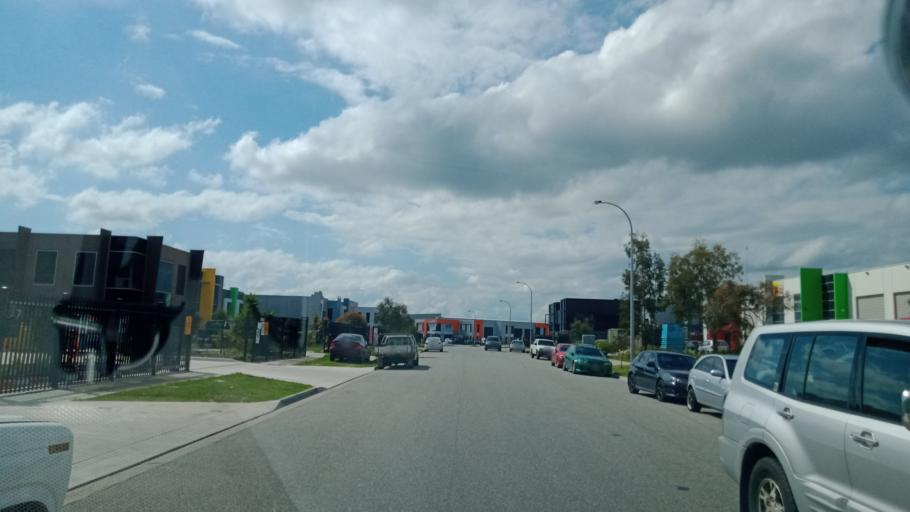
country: AU
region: Victoria
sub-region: Frankston
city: Carrum Downs
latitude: -38.0896
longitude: 145.1717
